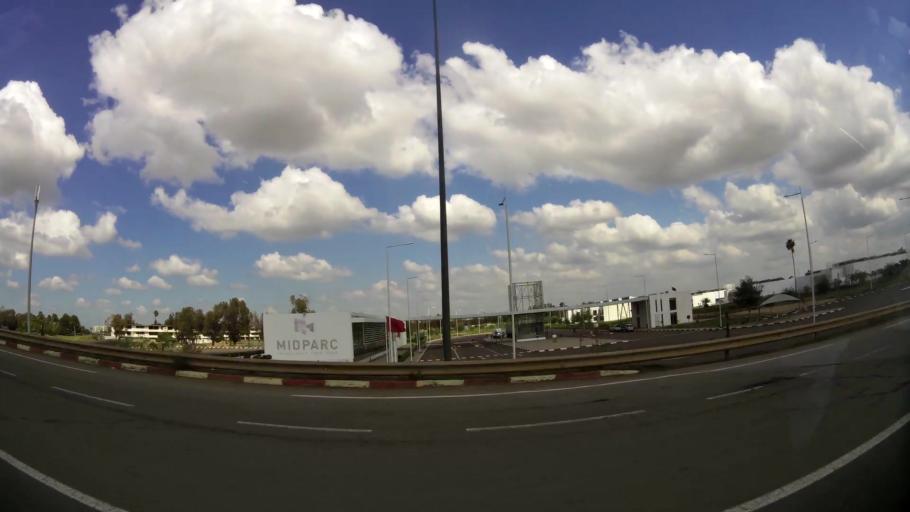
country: MA
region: Chaouia-Ouardigha
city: Nouaseur
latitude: 33.3762
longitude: -7.5684
